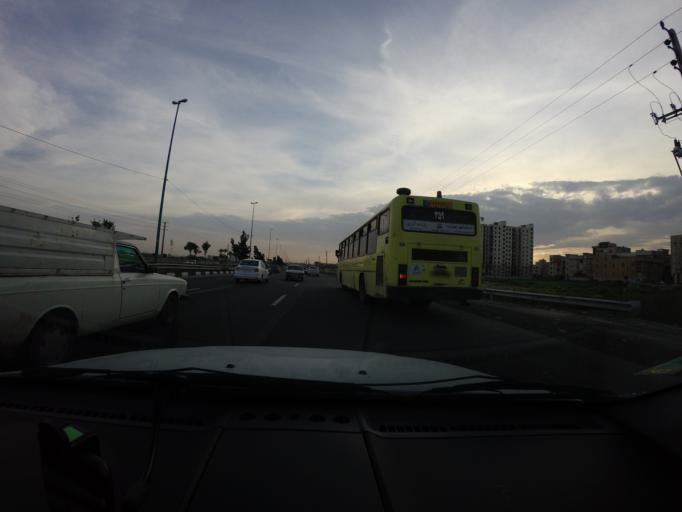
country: IR
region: Tehran
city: Eslamshahr
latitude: 35.5389
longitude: 51.2443
